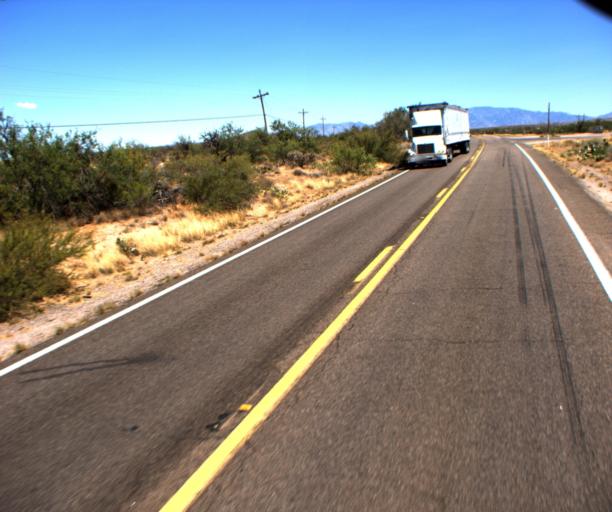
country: US
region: Arizona
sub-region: Pima County
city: Catalina
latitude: 32.6640
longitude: -111.0520
